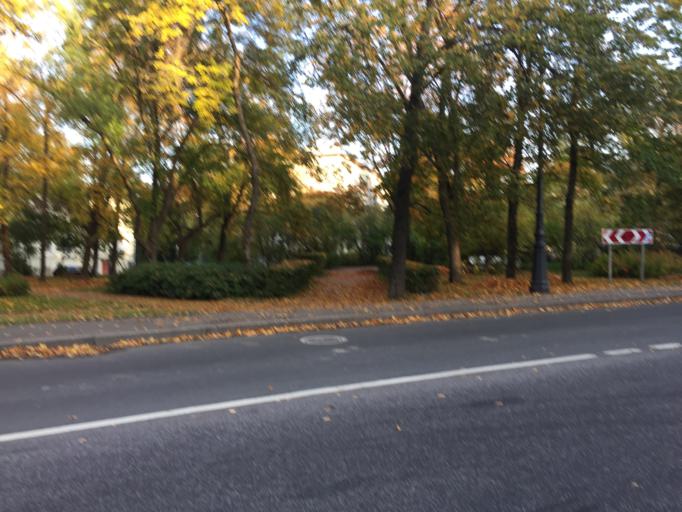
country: RU
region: St.-Petersburg
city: Pushkin
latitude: 59.7248
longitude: 30.3996
